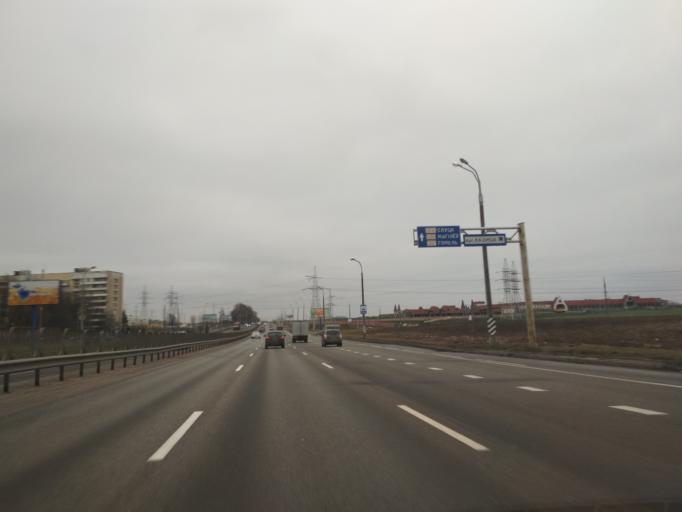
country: BY
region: Minsk
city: Yubilyeyny
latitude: 53.8391
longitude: 27.4956
